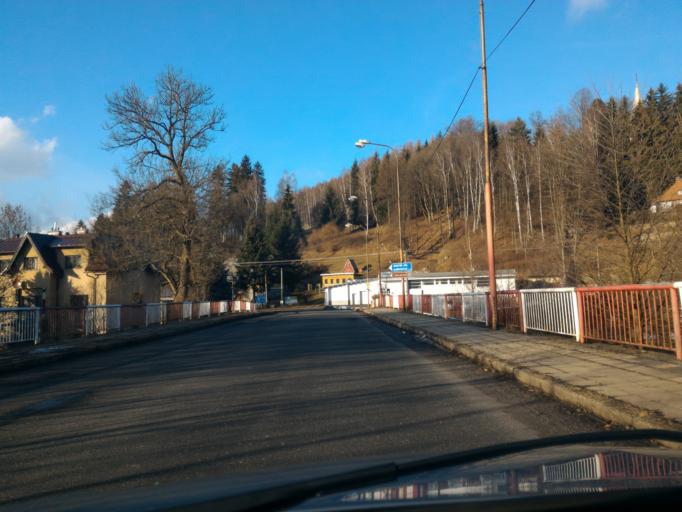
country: CZ
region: Liberecky
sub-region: Okres Jablonec nad Nisou
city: Tanvald
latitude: 50.7367
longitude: 15.2771
